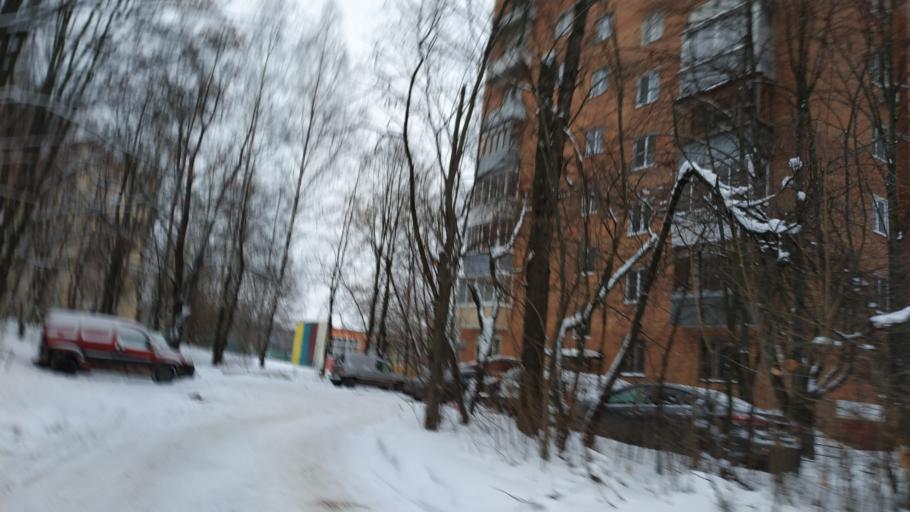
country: RU
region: Moskovskaya
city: Shchelkovo
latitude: 55.9315
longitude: 37.9933
